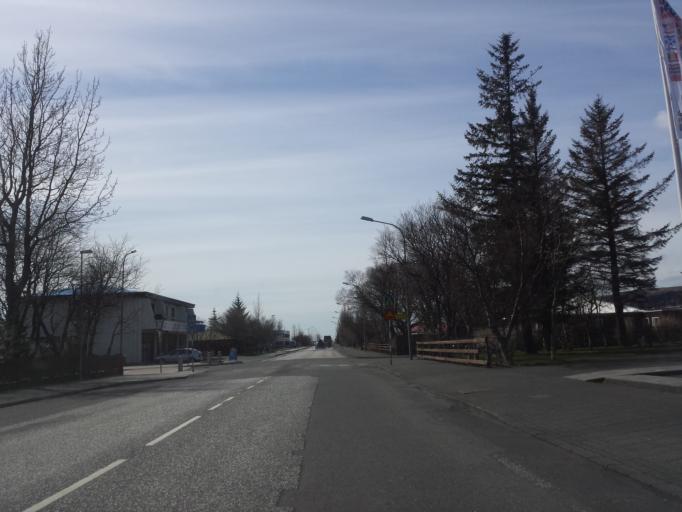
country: IS
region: South
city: Hveragerdi
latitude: 63.9995
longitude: -21.1872
